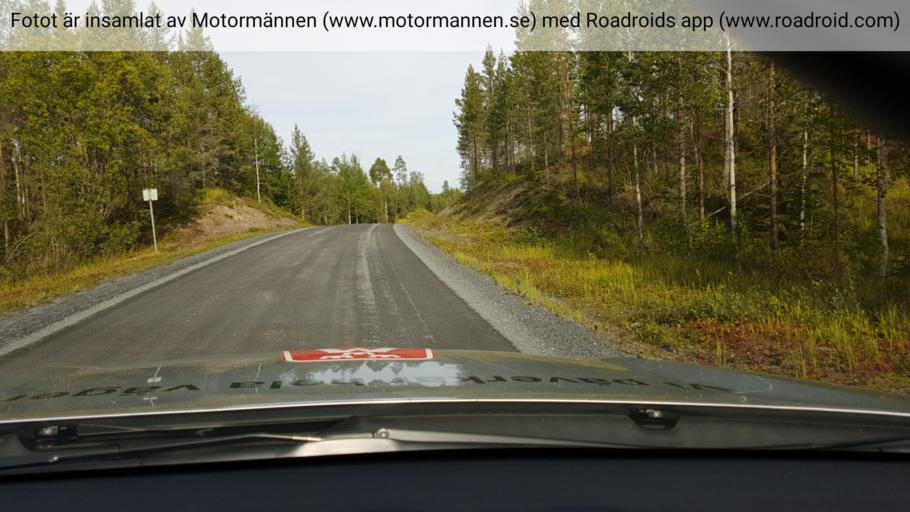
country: SE
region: Jaemtland
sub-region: Krokoms Kommun
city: Valla
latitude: 63.3111
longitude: 13.8340
